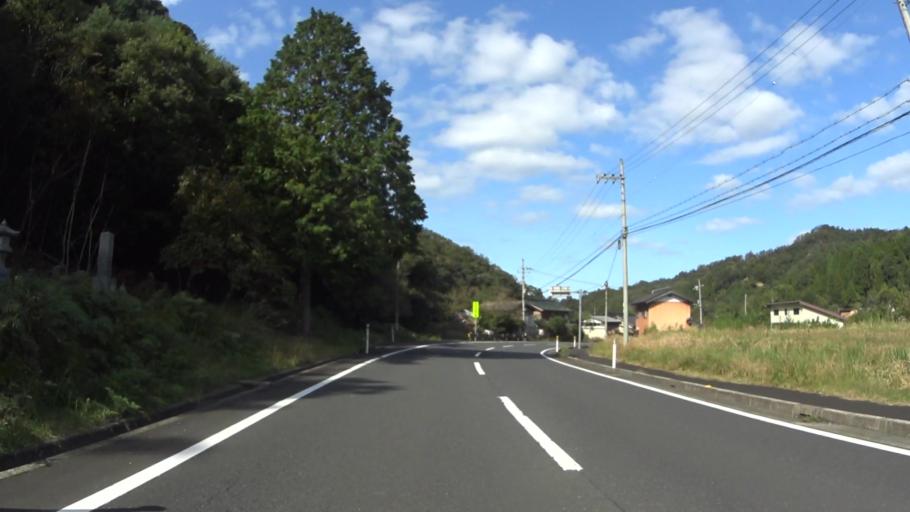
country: JP
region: Hyogo
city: Toyooka
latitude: 35.5606
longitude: 134.9790
